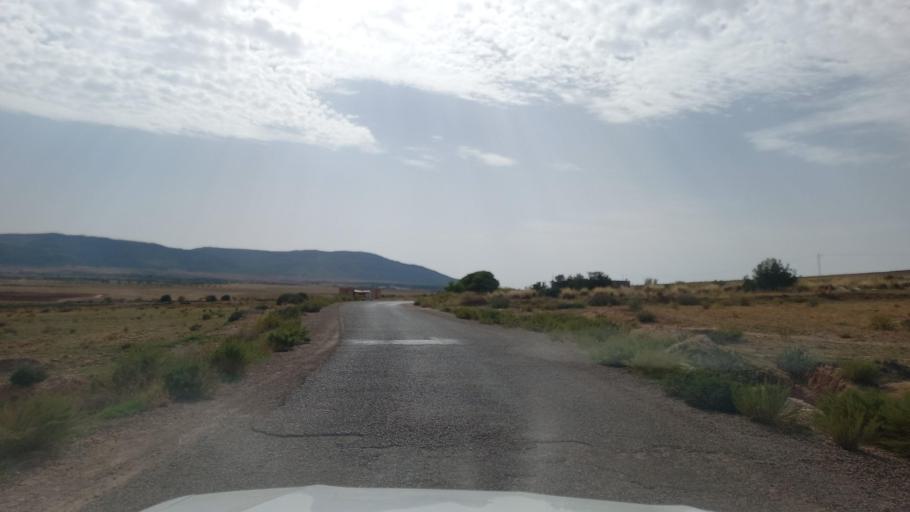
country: TN
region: Al Qasrayn
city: Kasserine
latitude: 35.3626
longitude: 8.8472
